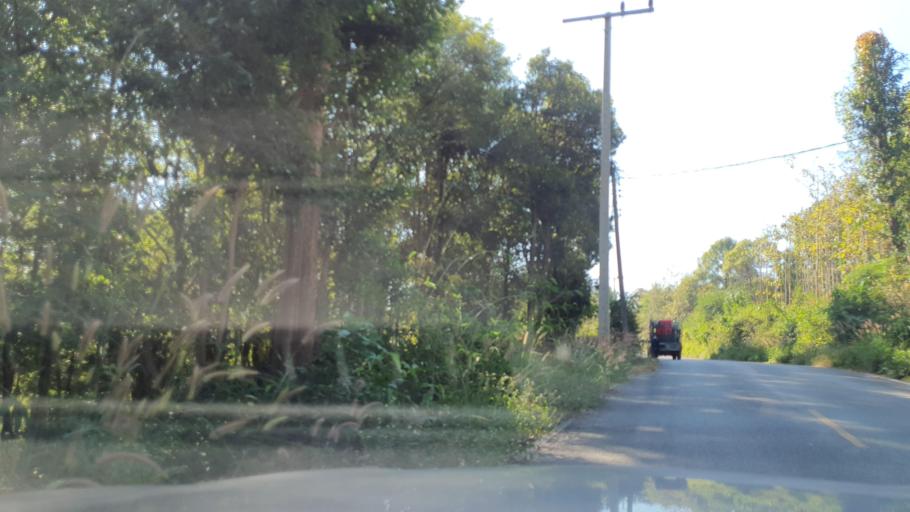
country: TH
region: Nan
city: Pua
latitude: 19.1702
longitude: 100.9097
